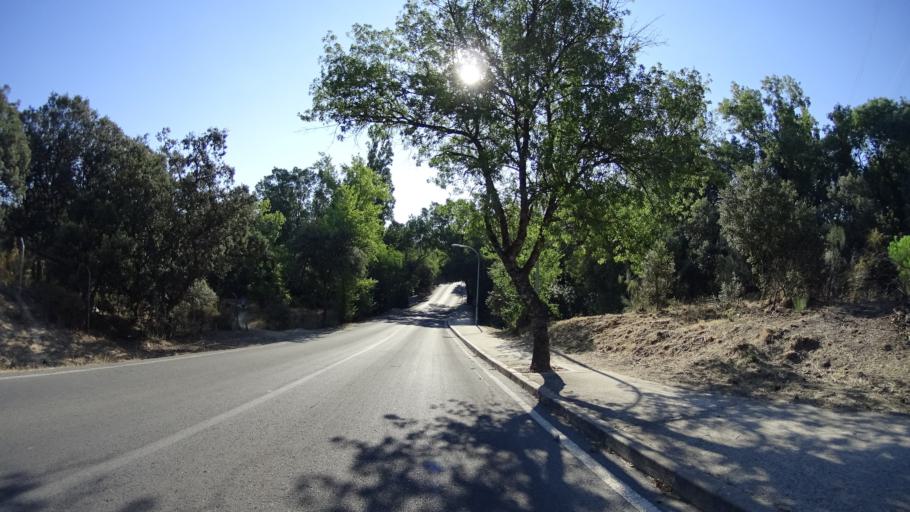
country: ES
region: Madrid
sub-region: Provincia de Madrid
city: Las Matas
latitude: 40.5829
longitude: -3.8961
